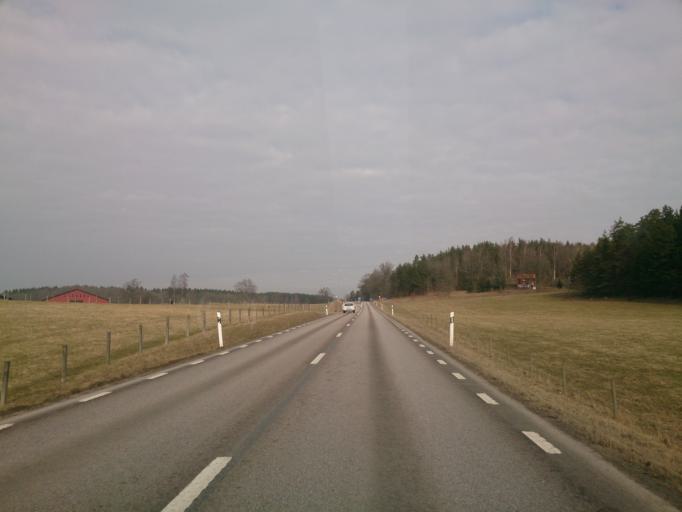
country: SE
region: OEstergoetland
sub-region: Atvidabergs Kommun
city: Atvidaberg
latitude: 58.2899
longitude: 15.8959
